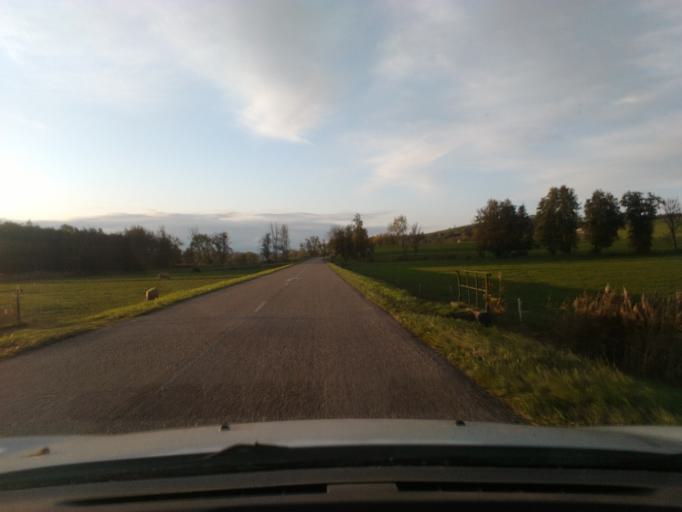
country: FR
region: Lorraine
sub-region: Departement des Vosges
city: Mirecourt
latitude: 48.2512
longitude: 6.2013
